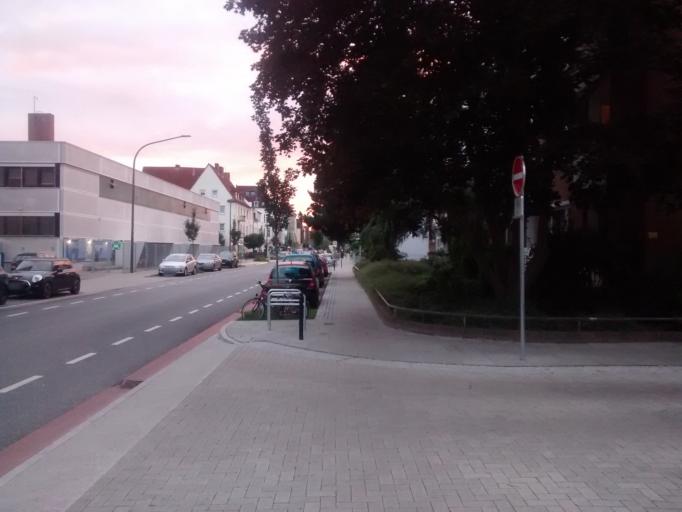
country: DE
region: Bremen
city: Bremen
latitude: 53.0946
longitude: 8.8036
